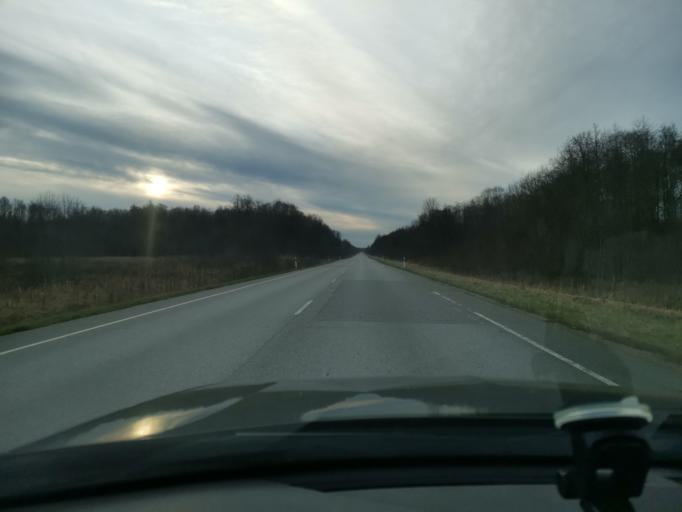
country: EE
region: Ida-Virumaa
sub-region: Narva-Joesuu linn
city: Narva-Joesuu
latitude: 59.3342
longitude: 27.9598
